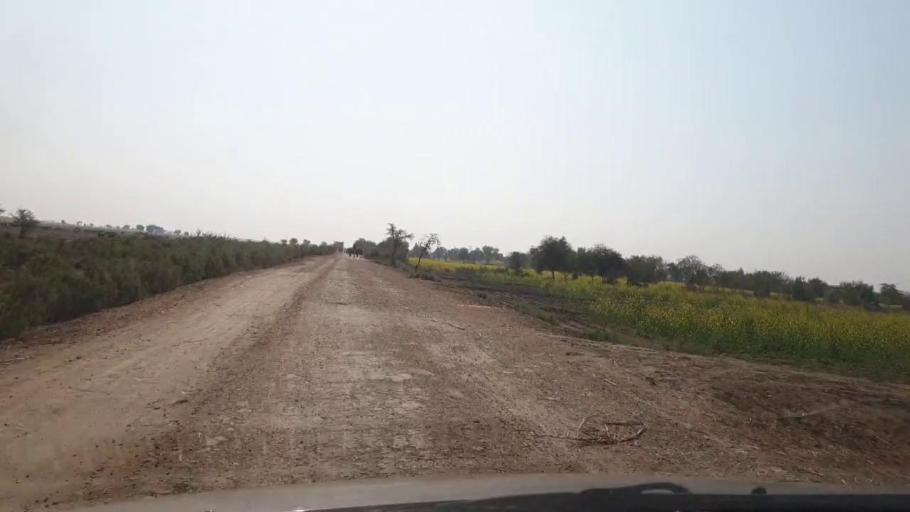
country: PK
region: Sindh
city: Jhol
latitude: 25.8832
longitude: 68.9971
